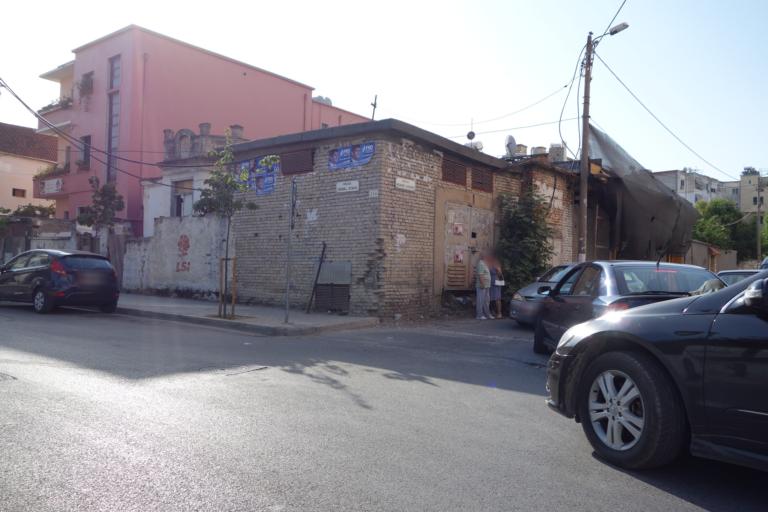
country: AL
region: Tirane
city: Tirana
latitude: 41.3323
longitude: 19.8276
